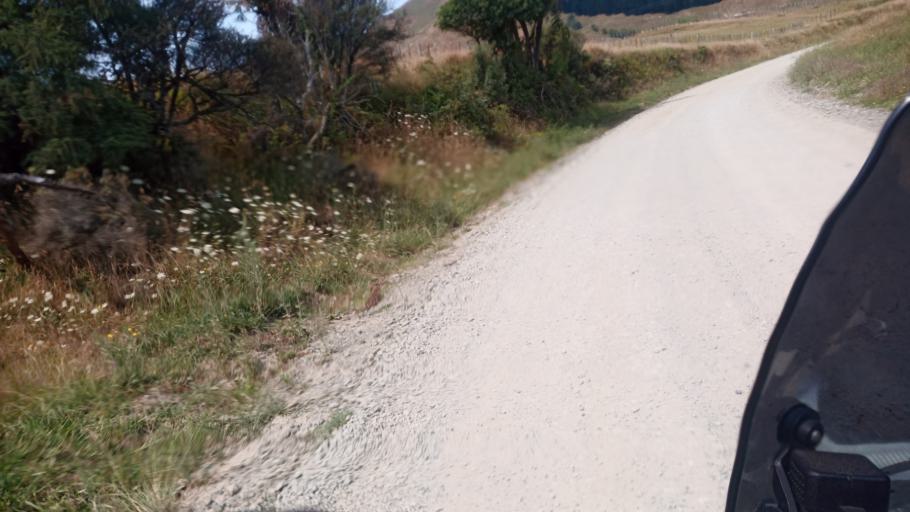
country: NZ
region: Bay of Plenty
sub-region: Opotiki District
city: Opotiki
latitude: -37.6565
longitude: 178.1231
